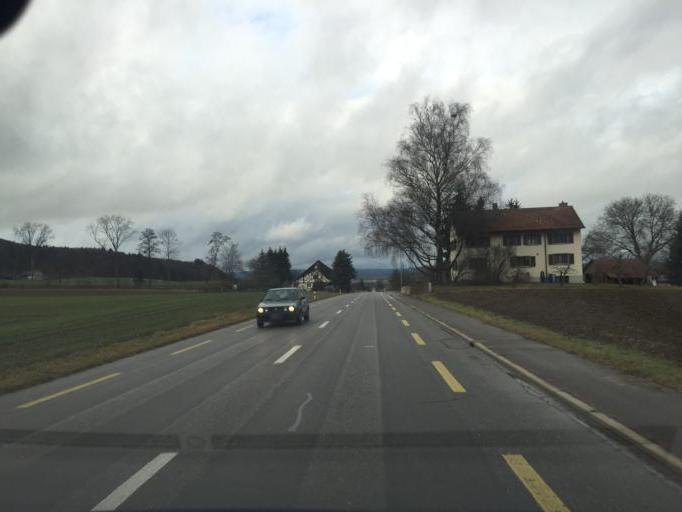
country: DE
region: Baden-Wuerttemberg
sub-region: Freiburg Region
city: Busingen
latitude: 47.6682
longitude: 8.6978
